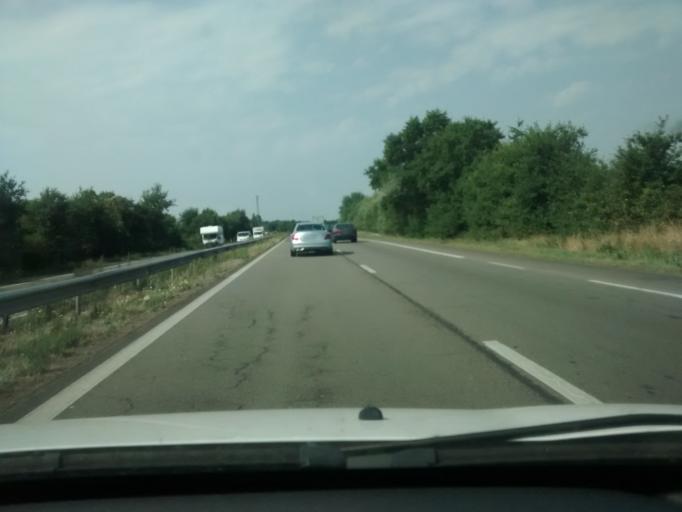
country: FR
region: Pays de la Loire
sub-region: Departement de la Loire-Atlantique
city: Donges
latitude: 47.3507
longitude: -2.0648
